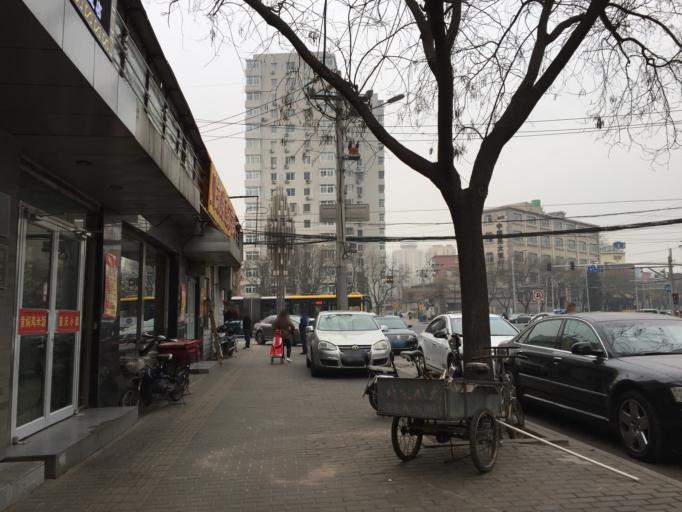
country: CN
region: Beijing
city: Chaowai
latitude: 39.9463
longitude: 116.4448
